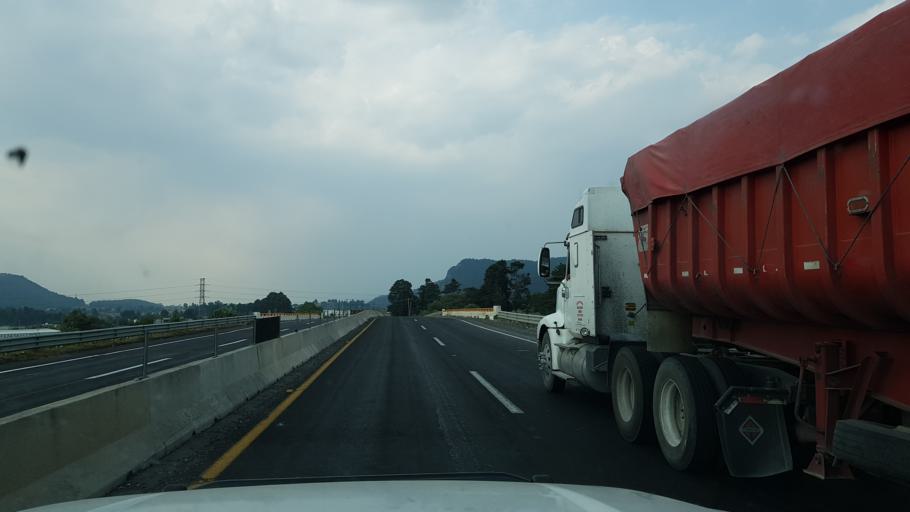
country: MX
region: Mexico
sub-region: Ayapango
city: La Colonia
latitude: 19.1442
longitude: -98.7760
